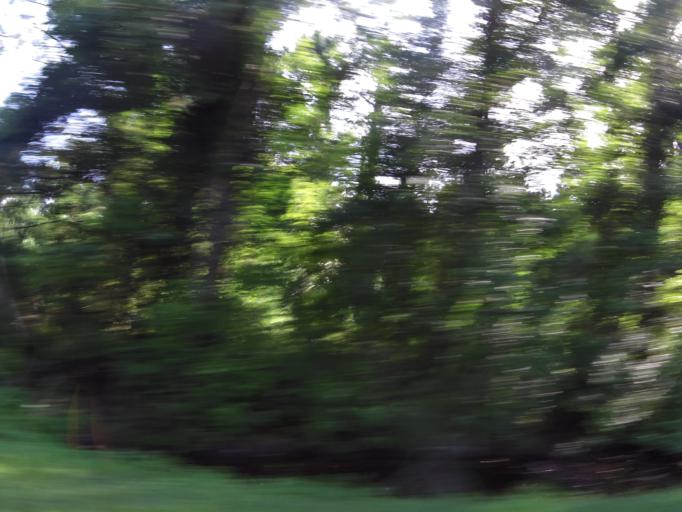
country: US
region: Florida
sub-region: Clay County
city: Green Cove Springs
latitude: 30.0131
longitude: -81.5590
